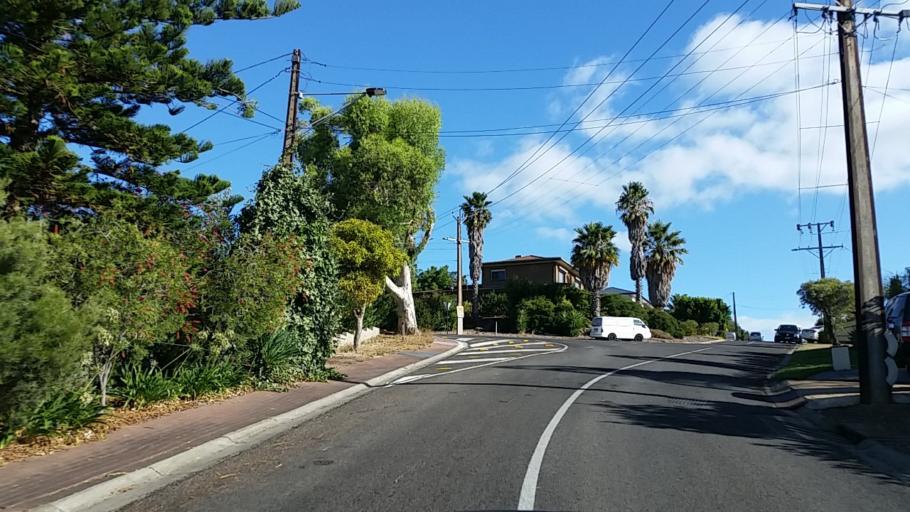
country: AU
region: South Australia
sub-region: Onkaparinga
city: Bedford Park
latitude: -35.0313
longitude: 138.5581
